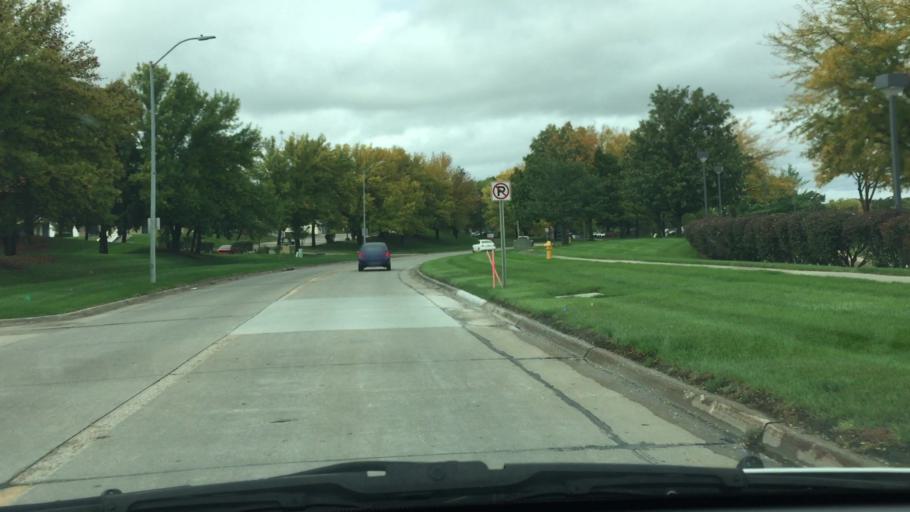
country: US
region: Iowa
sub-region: Polk County
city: Clive
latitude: 41.6046
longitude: -93.7737
